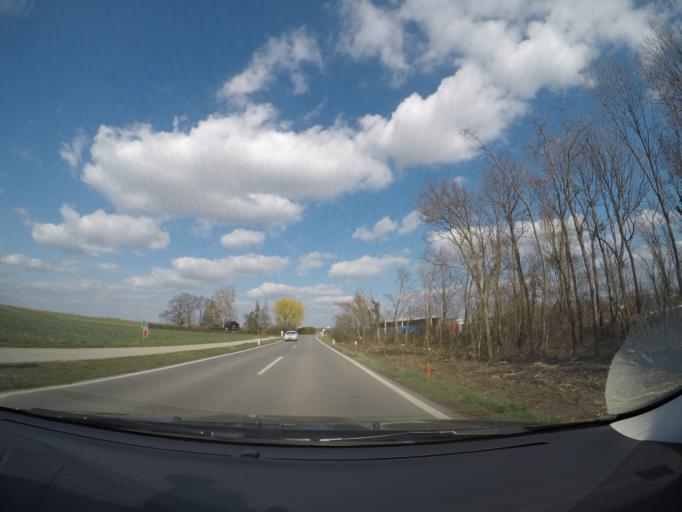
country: AT
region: Lower Austria
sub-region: Politischer Bezirk Wien-Umgebung
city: Schwadorf
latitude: 48.0758
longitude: 16.5900
